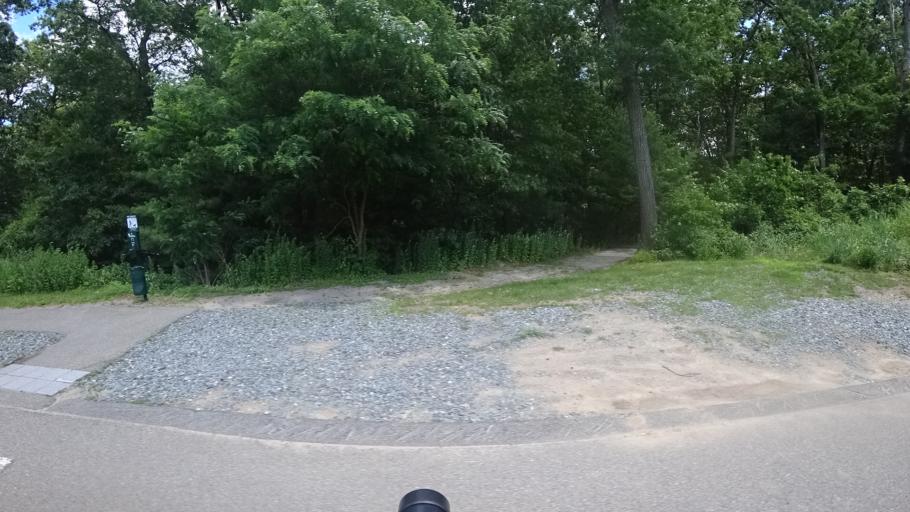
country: US
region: Massachusetts
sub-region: Norfolk County
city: Dedham
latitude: 42.2666
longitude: -71.1924
